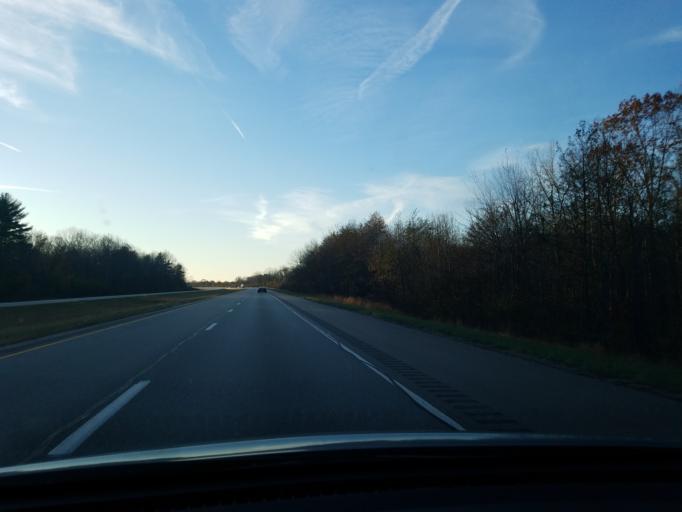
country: US
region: Indiana
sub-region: Gibson County
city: Oakland City
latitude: 38.1925
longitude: -87.3318
